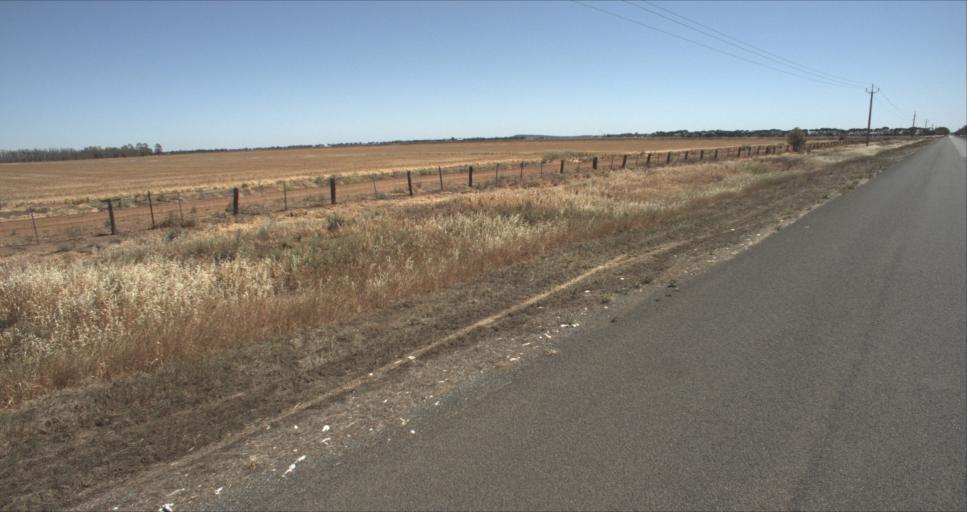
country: AU
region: New South Wales
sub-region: Leeton
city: Leeton
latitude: -34.4848
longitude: 146.2898
